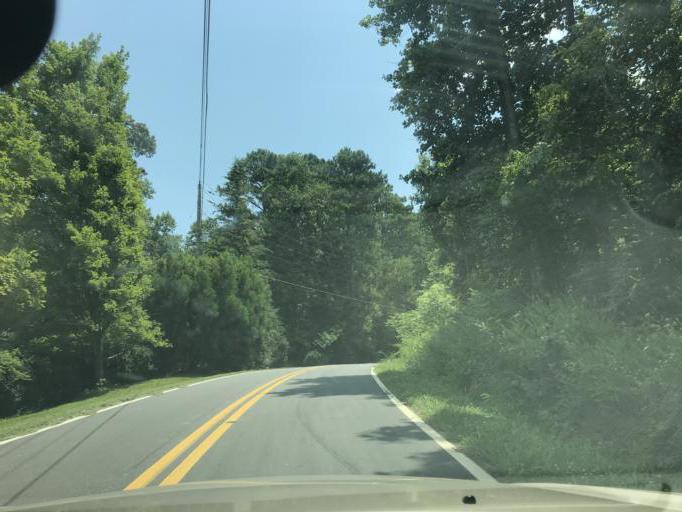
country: US
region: Georgia
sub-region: Forsyth County
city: Cumming
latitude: 34.3125
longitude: -84.1990
